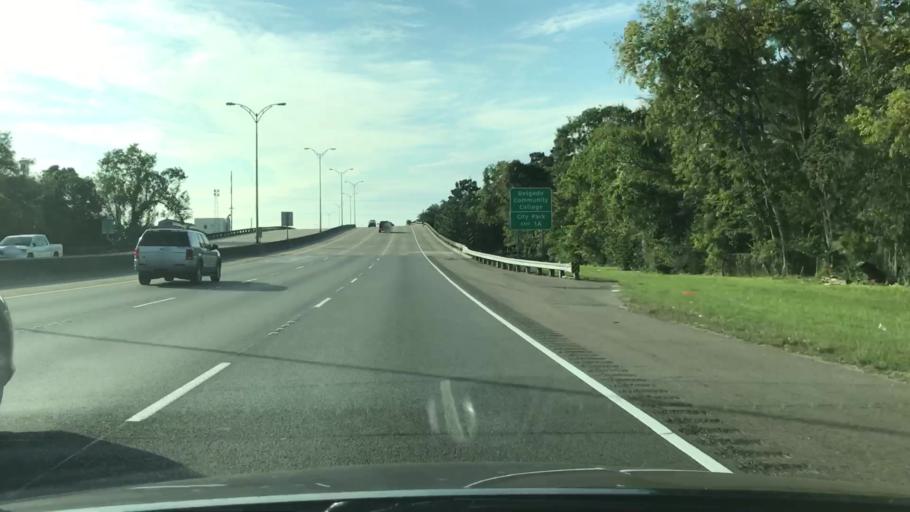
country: US
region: Louisiana
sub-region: Orleans Parish
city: New Orleans
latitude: 29.9944
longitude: -90.0982
